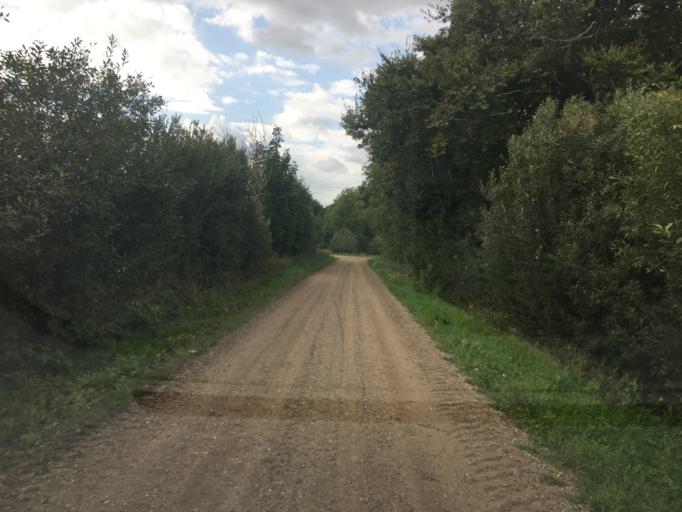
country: DK
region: South Denmark
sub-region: Tonder Kommune
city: Logumkloster
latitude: 55.0059
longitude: 8.9496
